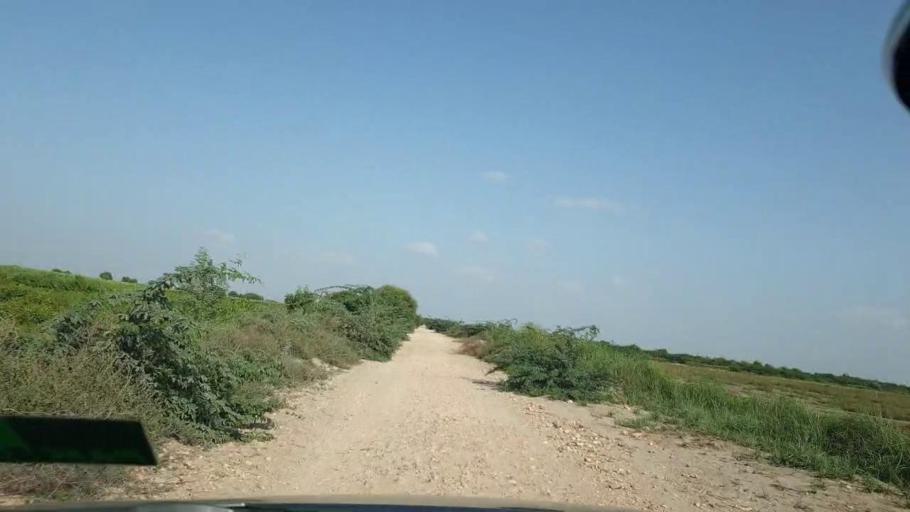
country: PK
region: Sindh
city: Naukot
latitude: 24.7031
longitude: 69.2051
